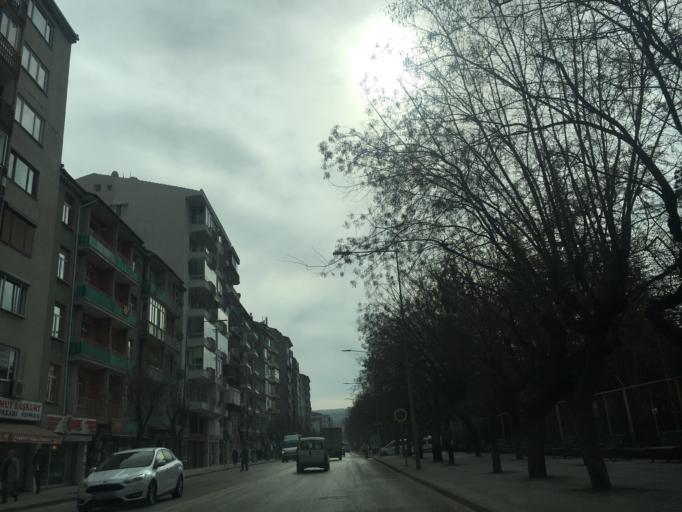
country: TR
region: Eskisehir
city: Eskisehir
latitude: 39.7728
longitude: 30.5136
